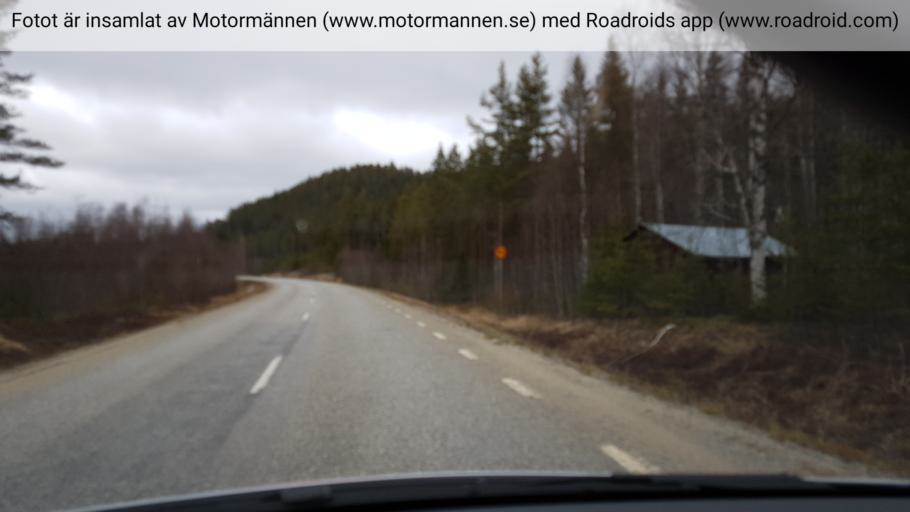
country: SE
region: Vaesternorrland
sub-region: OErnskoeldsviks Kommun
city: Bredbyn
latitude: 63.9324
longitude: 18.4816
